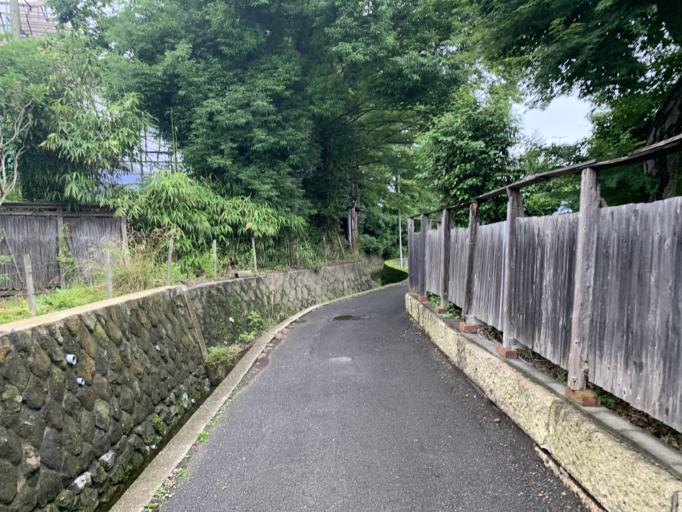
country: JP
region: Tochigi
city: Tochigi
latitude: 36.3861
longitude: 139.7325
